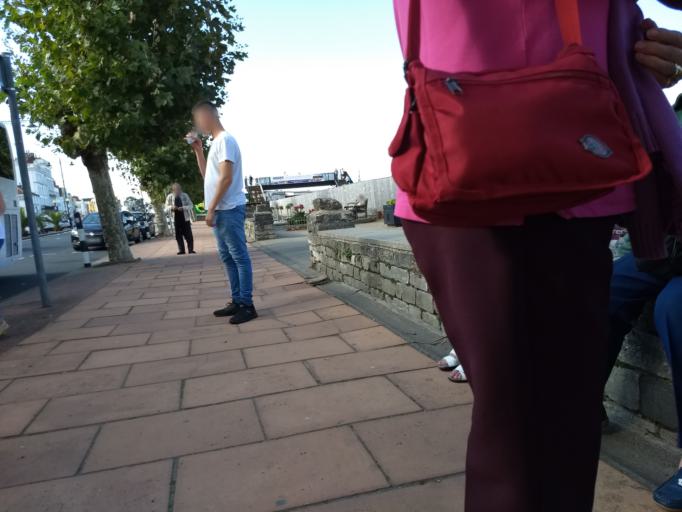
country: GB
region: England
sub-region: Isle of Wight
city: Ryde
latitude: 50.7321
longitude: -1.1578
